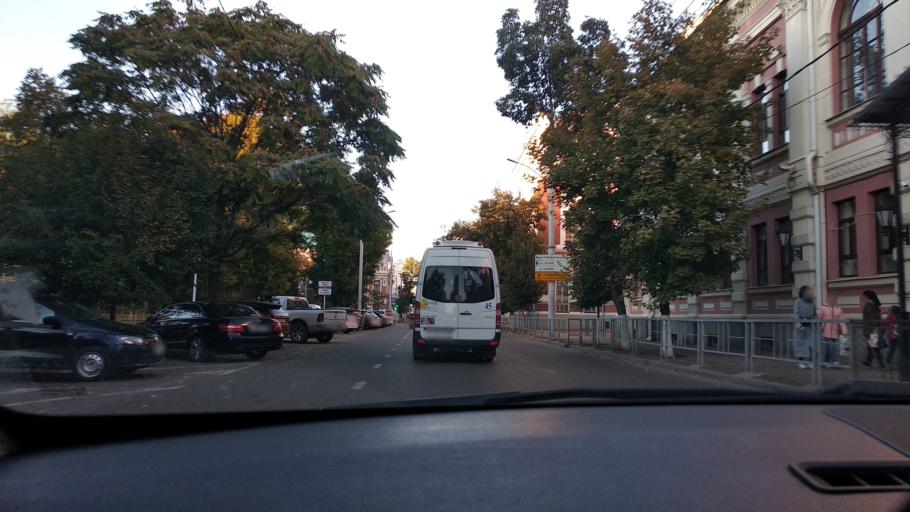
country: RU
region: Krasnodarskiy
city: Krasnodar
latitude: 45.0239
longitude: 38.9724
